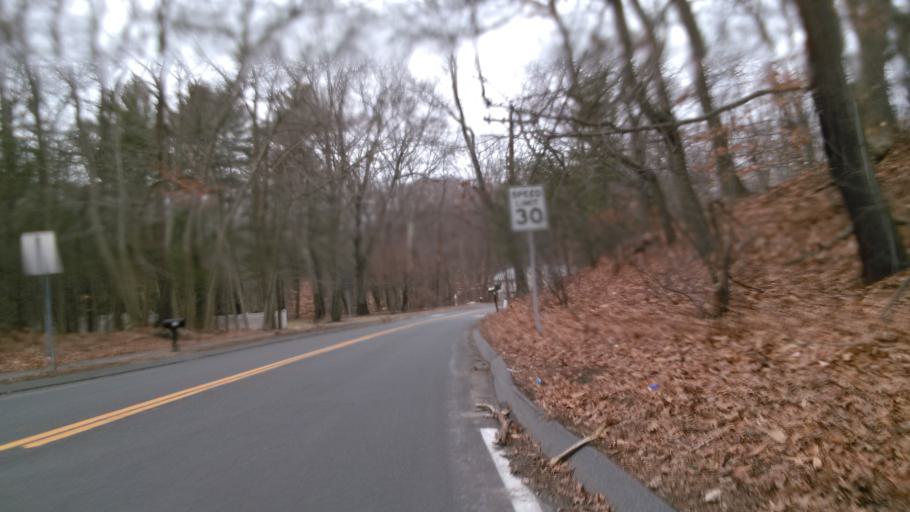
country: US
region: Massachusetts
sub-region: Middlesex County
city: Lexington
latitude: 42.4772
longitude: -71.2405
